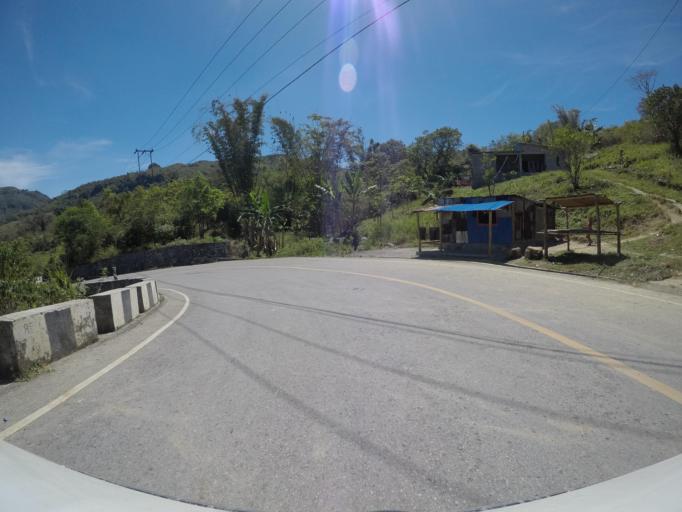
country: TL
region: Manatuto
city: Manatuto
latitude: -8.7793
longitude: 125.9682
